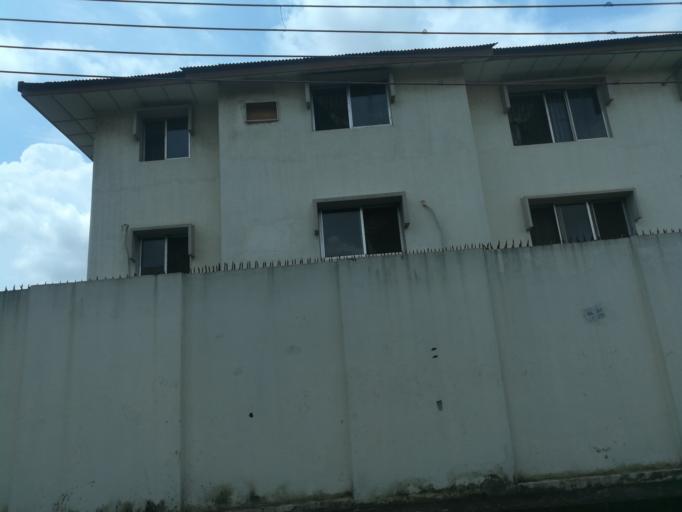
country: NG
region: Lagos
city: Somolu
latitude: 6.5364
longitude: 3.3662
